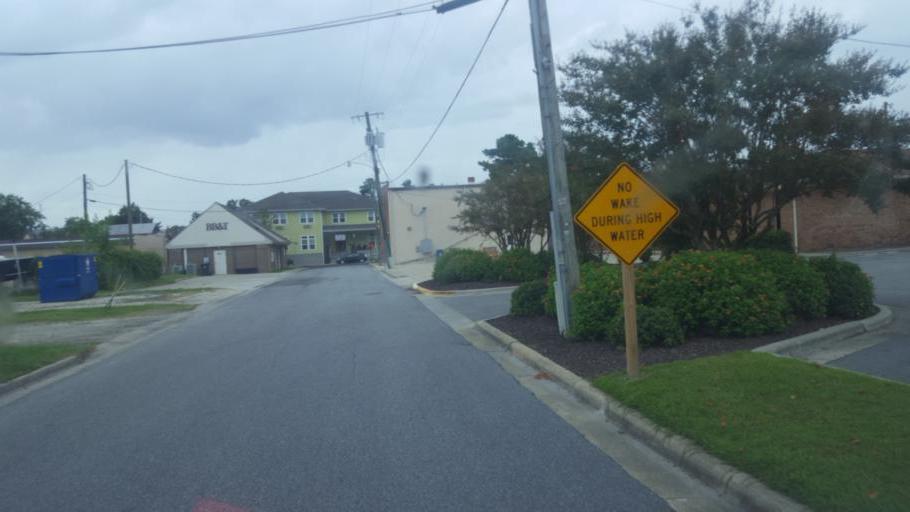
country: US
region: North Carolina
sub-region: Tyrrell County
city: Columbia
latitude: 35.9167
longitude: -76.2536
